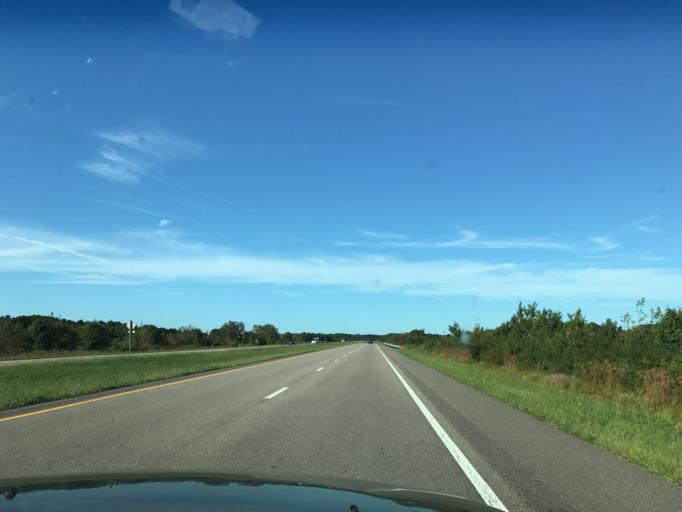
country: US
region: Virginia
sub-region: City of Portsmouth
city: Portsmouth Heights
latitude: 36.6916
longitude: -76.3463
